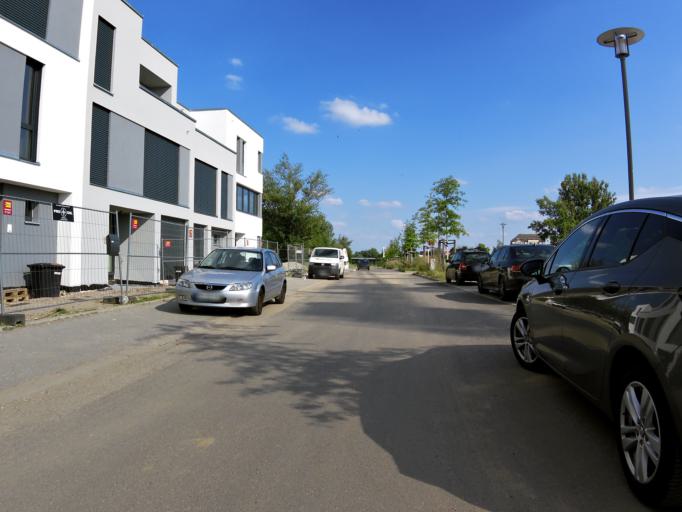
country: DE
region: Saxony
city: Leipzig
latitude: 51.3312
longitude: 12.3054
